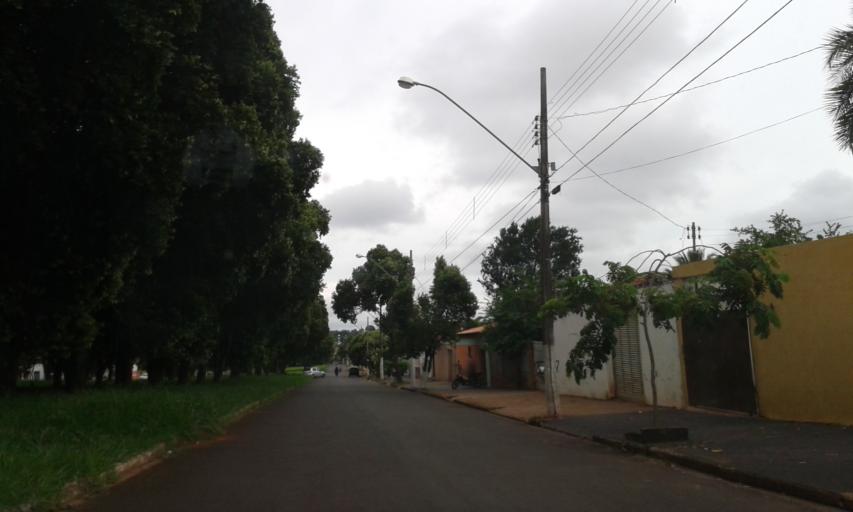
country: BR
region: Minas Gerais
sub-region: Ituiutaba
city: Ituiutaba
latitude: -18.9819
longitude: -49.4523
